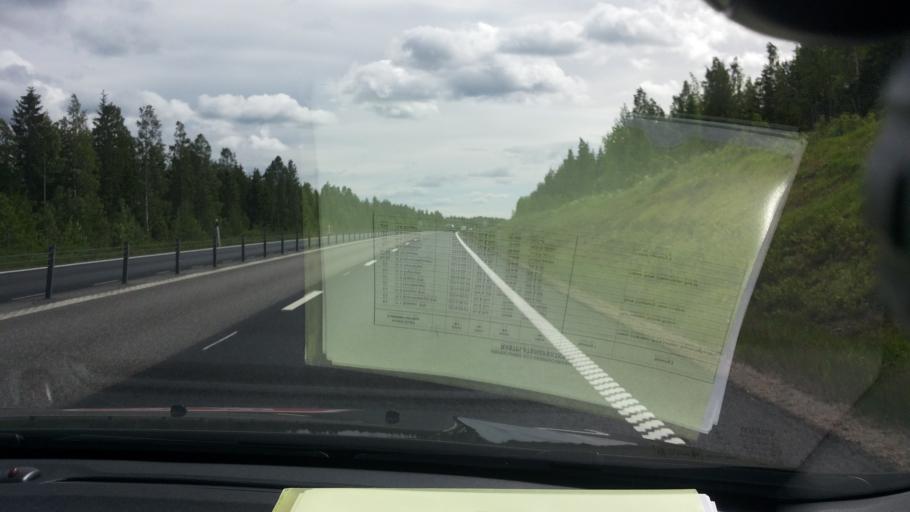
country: SE
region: Vaesternorrland
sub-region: Sundsvalls Kommun
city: Njurundabommen
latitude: 62.1805
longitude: 17.3565
